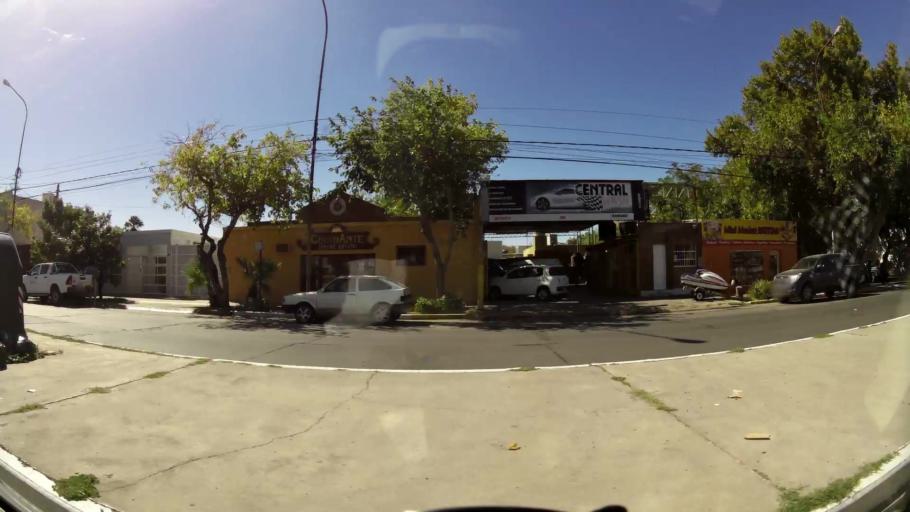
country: AR
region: San Juan
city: San Juan
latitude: -31.5378
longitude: -68.5409
